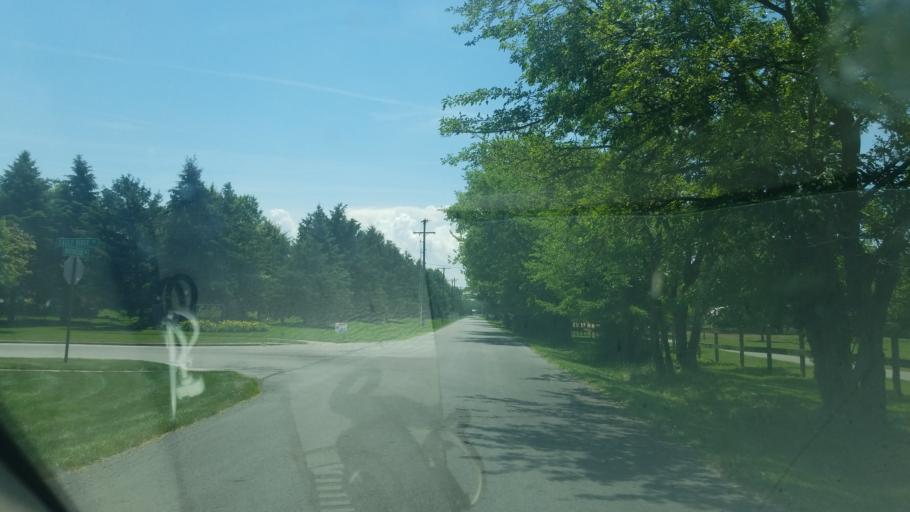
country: US
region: Ohio
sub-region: Hancock County
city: Findlay
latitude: 41.0146
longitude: -83.6355
